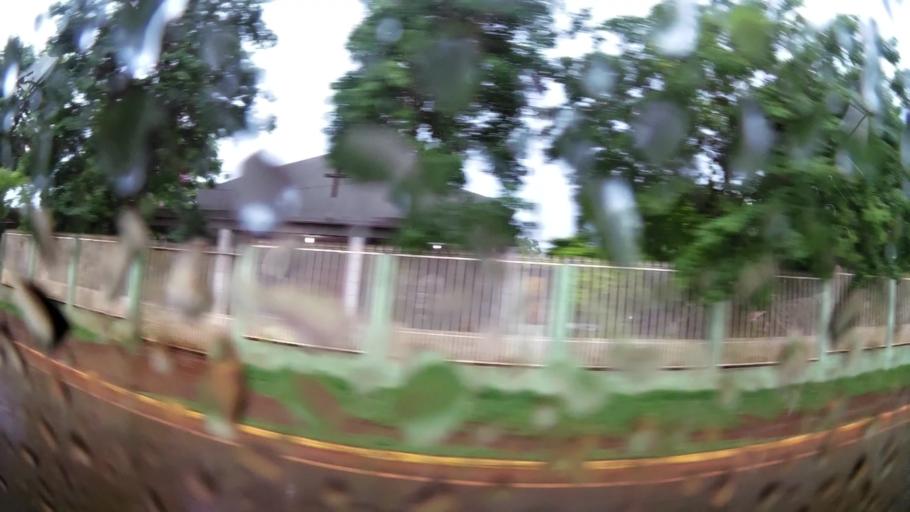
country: PY
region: Alto Parana
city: Presidente Franco
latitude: -25.5400
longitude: -54.6782
